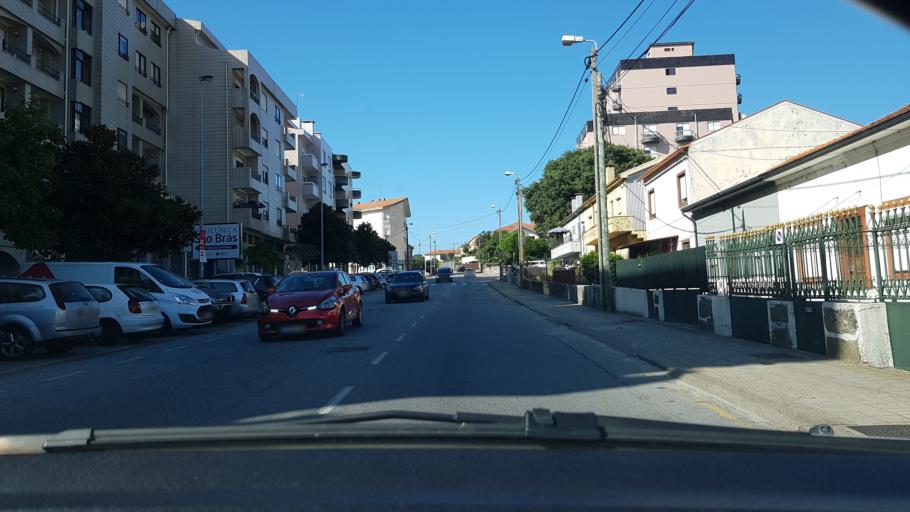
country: PT
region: Porto
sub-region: Gondomar
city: Baguim do Monte
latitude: 41.1862
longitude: -8.5400
